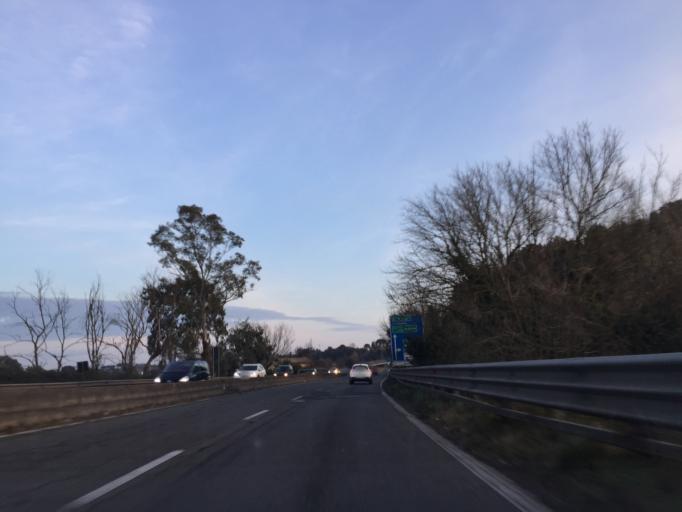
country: IT
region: Latium
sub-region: Citta metropolitana di Roma Capitale
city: Monte Caminetto
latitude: 41.9938
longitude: 12.4668
